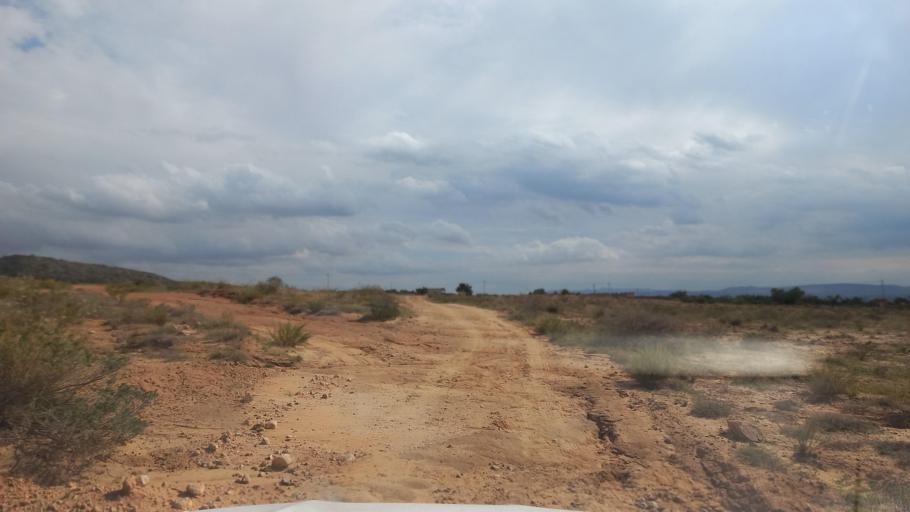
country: TN
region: Al Qasrayn
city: Sbiba
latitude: 35.2992
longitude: 9.1202
